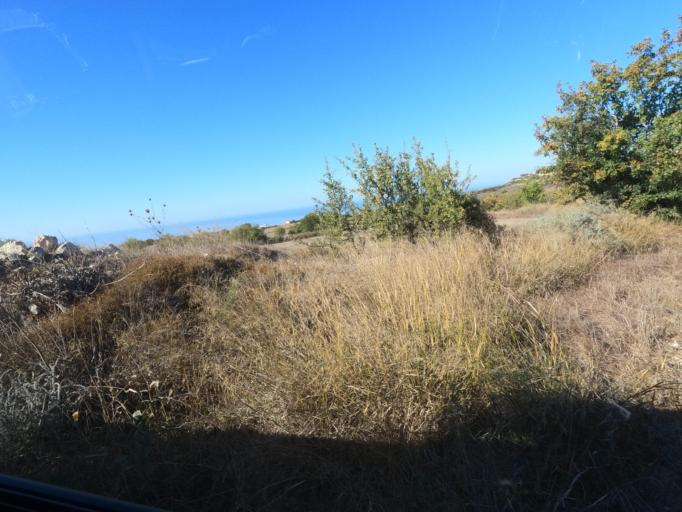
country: CY
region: Pafos
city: Mesogi
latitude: 34.8015
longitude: 32.4931
